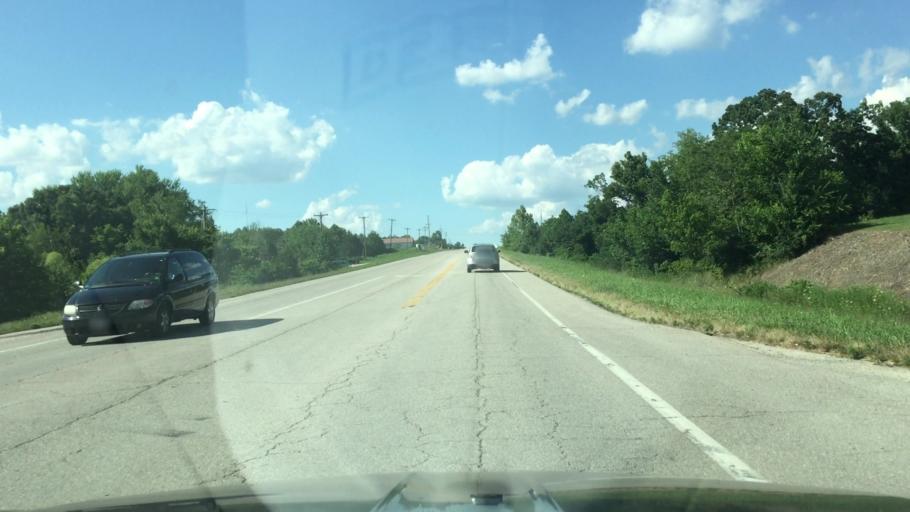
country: US
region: Missouri
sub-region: Miller County
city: Eldon
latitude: 38.3233
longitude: -92.5877
